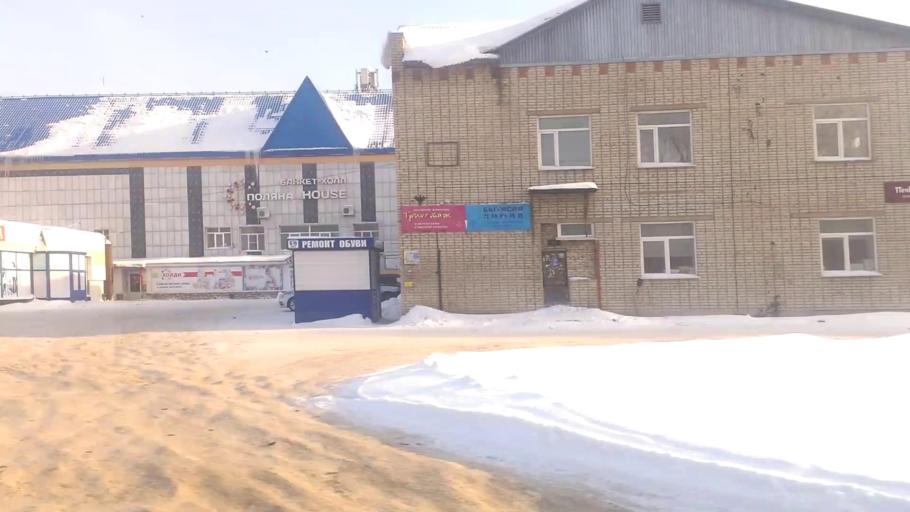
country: RU
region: Altai Krai
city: Novosilikatnyy
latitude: 53.3710
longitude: 83.6624
